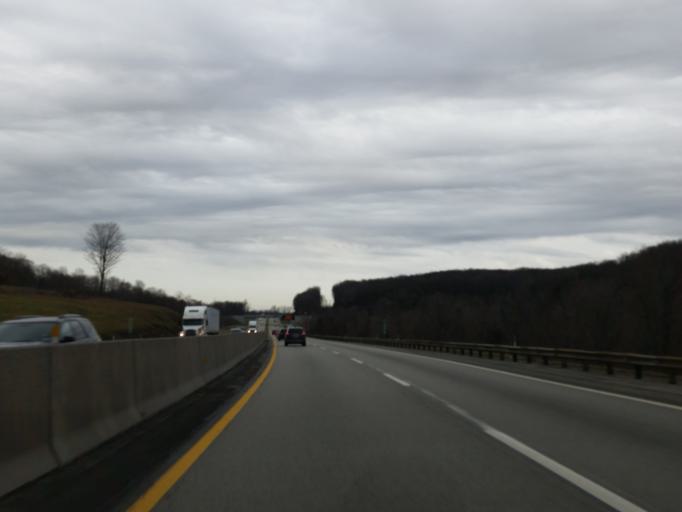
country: US
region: Pennsylvania
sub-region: Somerset County
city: Somerset
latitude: 40.0679
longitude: -79.1543
